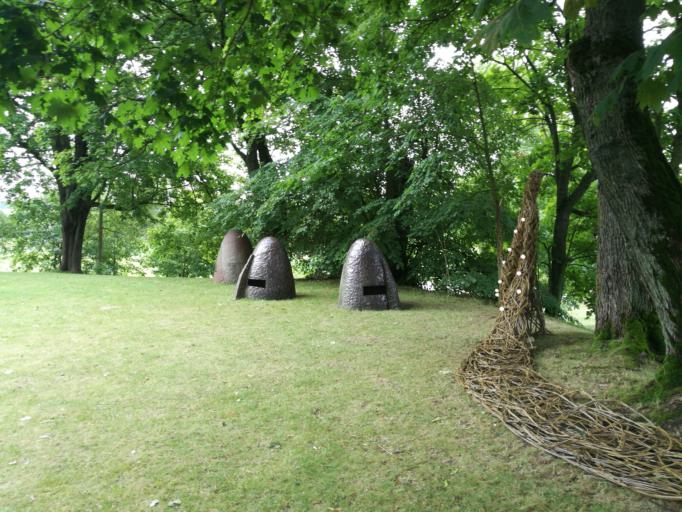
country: LT
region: Kauno apskritis
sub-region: Kaunas
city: Sargenai
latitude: 55.0651
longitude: 23.7928
